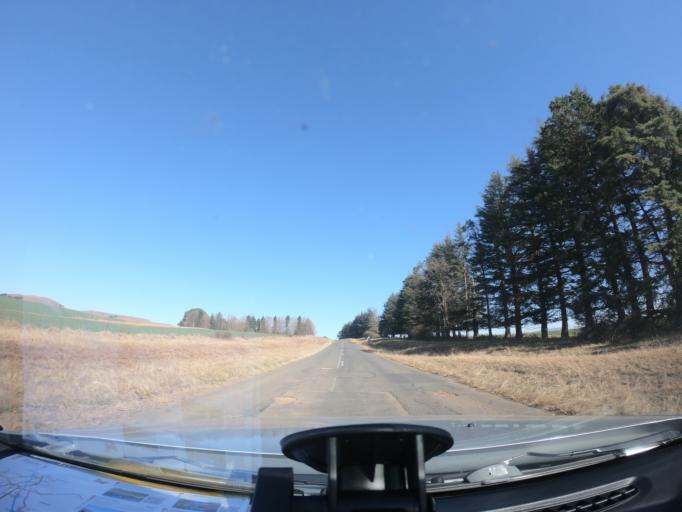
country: ZA
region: KwaZulu-Natal
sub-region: uMgungundlovu District Municipality
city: Mooirivier
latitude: -29.3276
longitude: 29.8263
